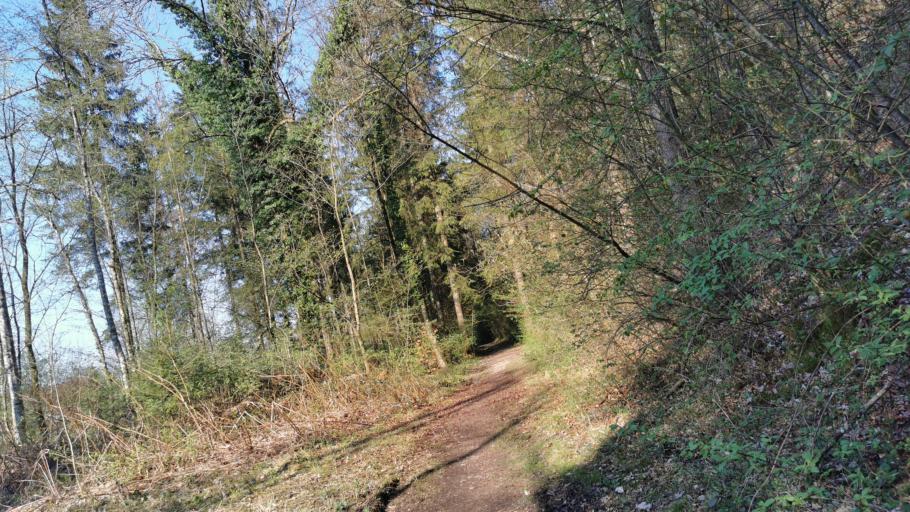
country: AT
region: Salzburg
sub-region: Politischer Bezirk Salzburg-Umgebung
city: Grodig
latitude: 47.7462
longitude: 12.9995
